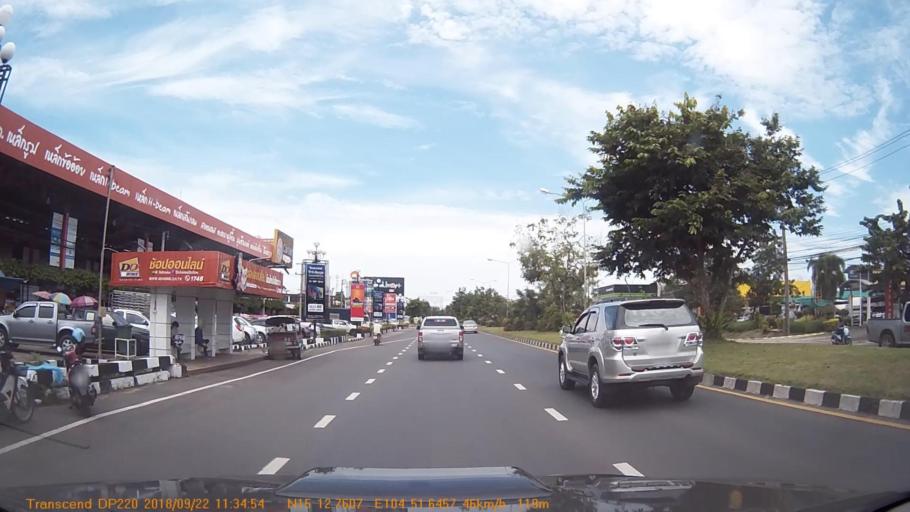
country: TH
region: Changwat Ubon Ratchathani
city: Warin Chamrap
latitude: 15.2127
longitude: 104.8607
